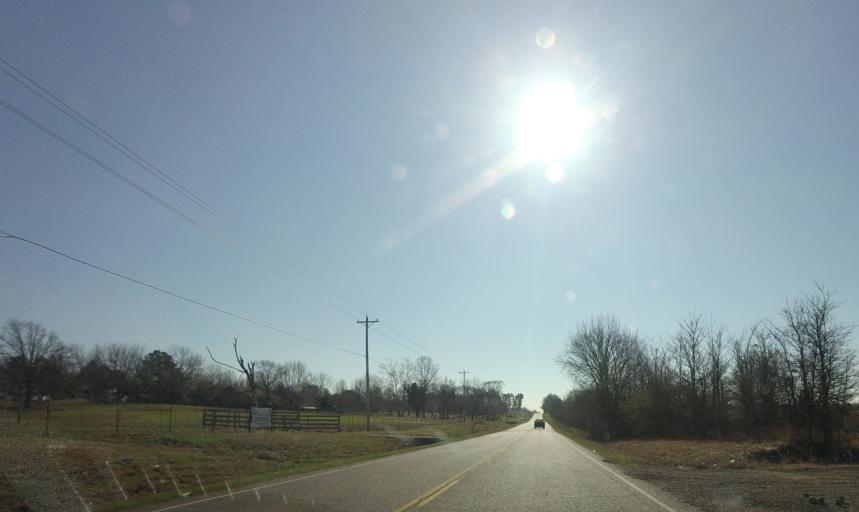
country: US
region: Tennessee
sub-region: Shelby County
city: Collierville
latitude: 34.9743
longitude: -89.6889
